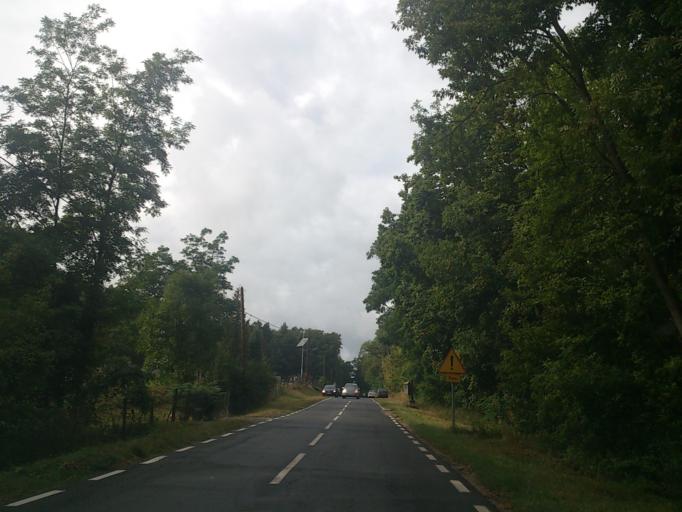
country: PL
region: Greater Poland Voivodeship
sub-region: Powiat poznanski
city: Pobiedziska
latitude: 52.5068
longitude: 17.2079
